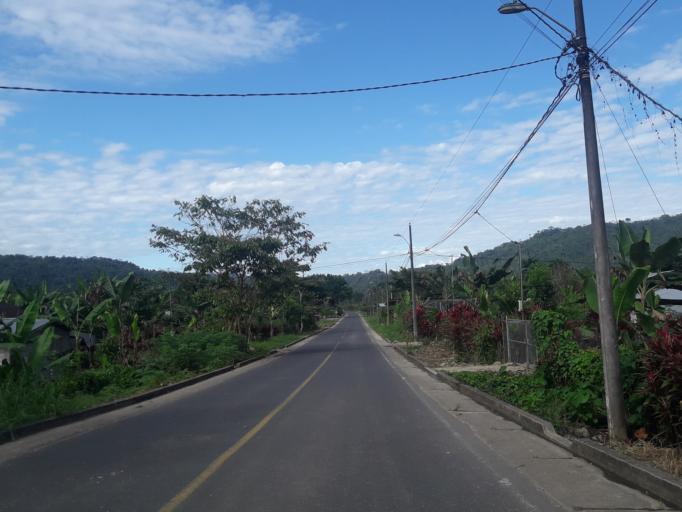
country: EC
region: Napo
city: Tena
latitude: -0.9748
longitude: -77.8406
